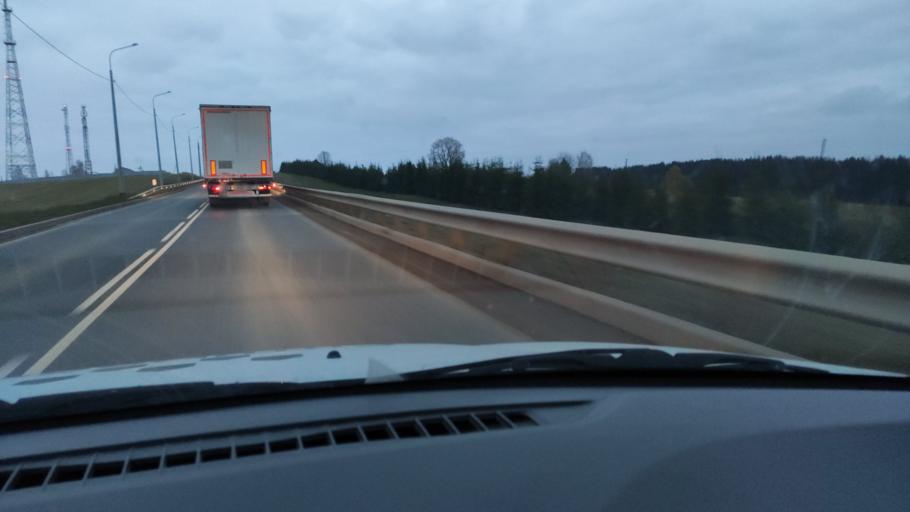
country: RU
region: Kirov
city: Kostino
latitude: 58.8509
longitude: 53.2804
